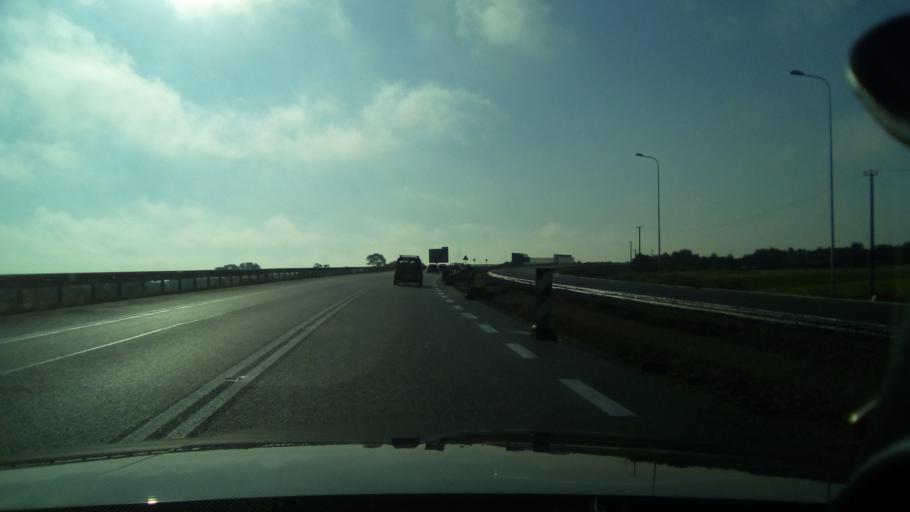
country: PL
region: Silesian Voivodeship
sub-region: Powiat bedzinski
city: Mierzecice
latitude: 50.4493
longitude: 19.1339
